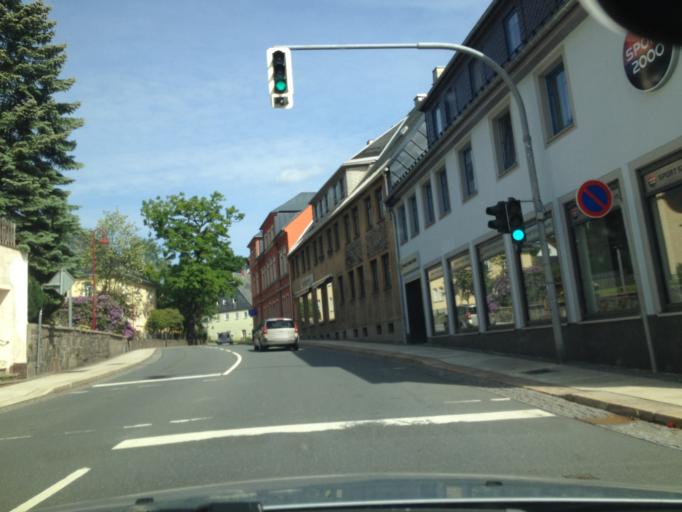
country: DE
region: Saxony
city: Thum
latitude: 50.6711
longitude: 12.9509
